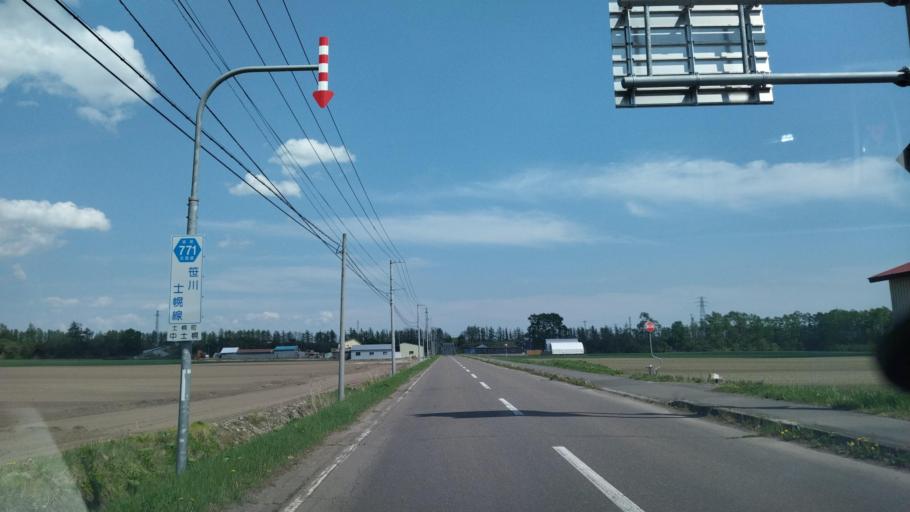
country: JP
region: Hokkaido
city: Otofuke
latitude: 43.1019
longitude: 143.2149
